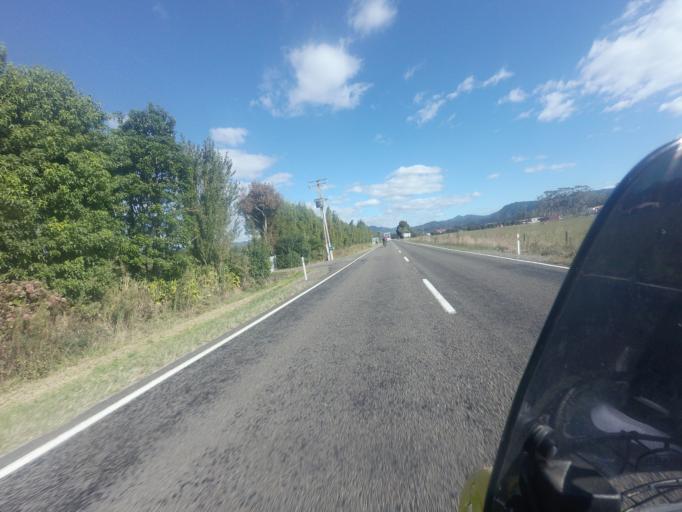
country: NZ
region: Bay of Plenty
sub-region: Opotiki District
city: Opotiki
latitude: -38.0376
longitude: 177.2901
